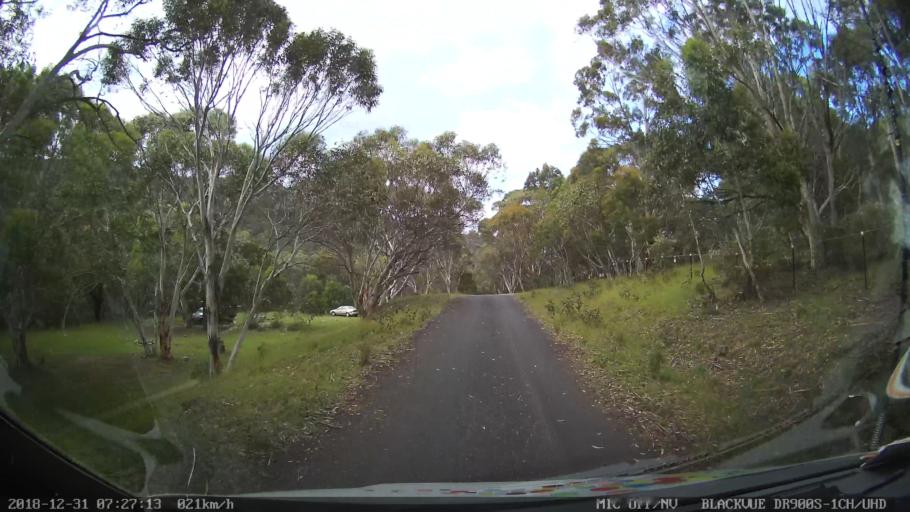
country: AU
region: New South Wales
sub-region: Snowy River
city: Jindabyne
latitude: -36.3206
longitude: 148.4804
